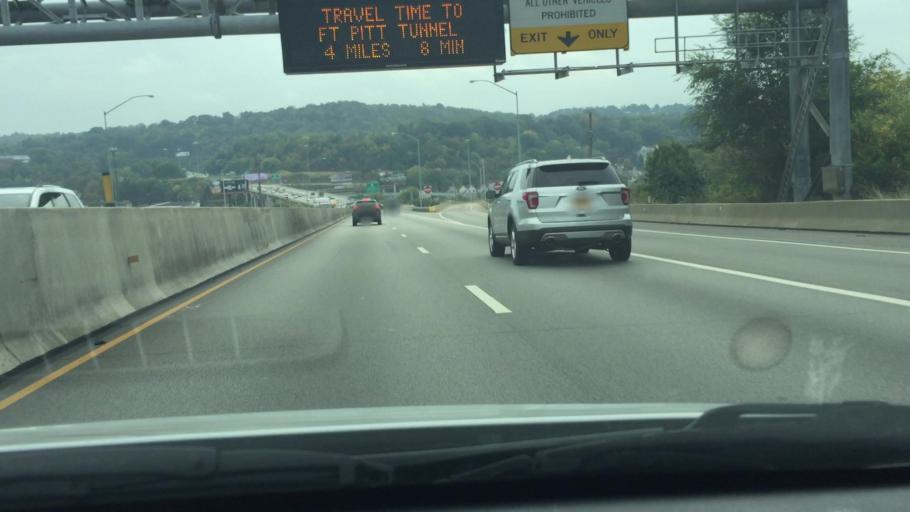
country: US
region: Pennsylvania
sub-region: Allegheny County
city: Carnegie
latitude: 40.4163
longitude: -80.0856
